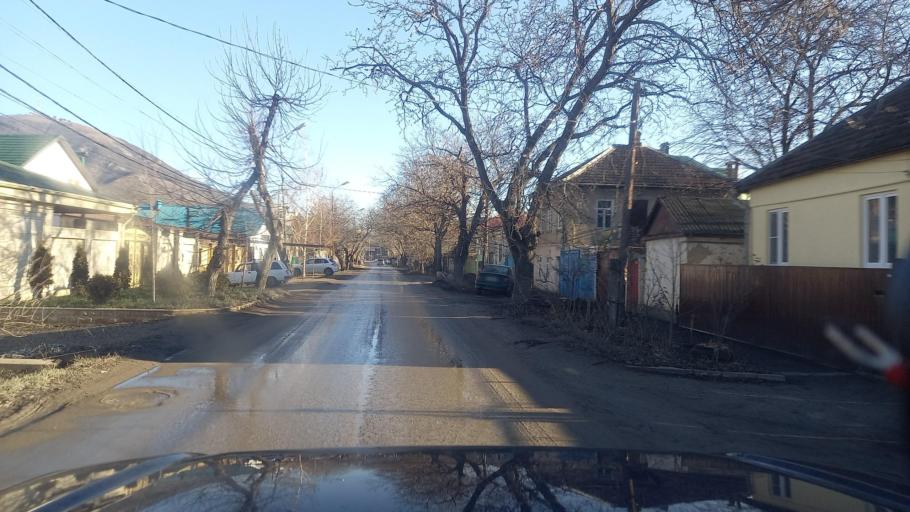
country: RU
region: Stavropol'skiy
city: Svobody
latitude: 44.0255
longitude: 43.0702
